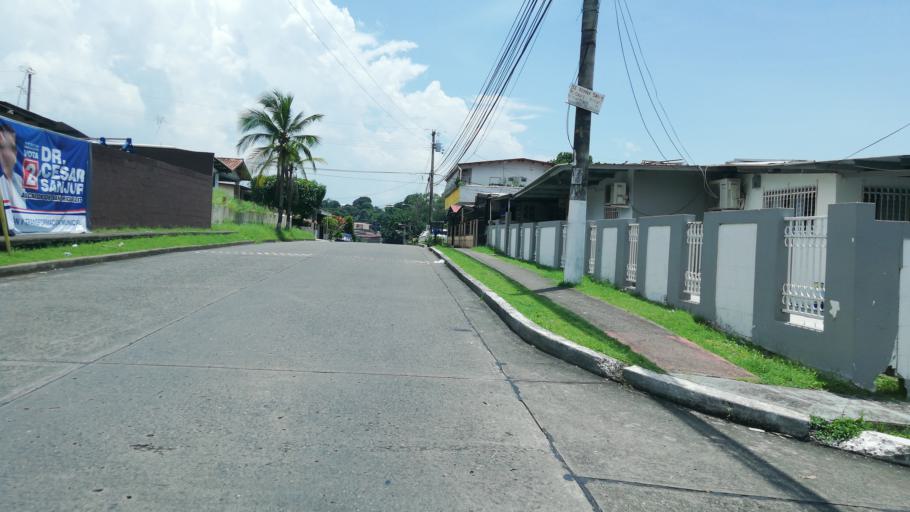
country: PA
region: Panama
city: San Miguelito
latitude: 9.0606
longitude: -79.4565
